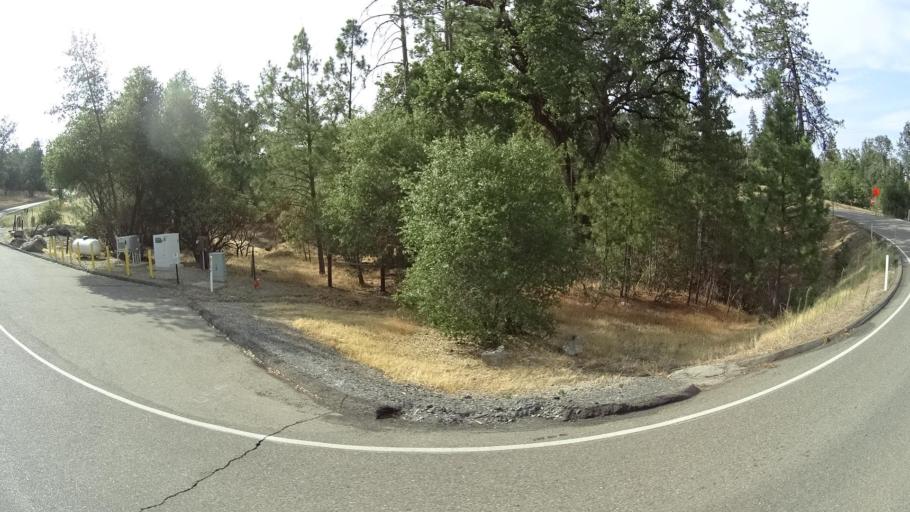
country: US
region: California
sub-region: Madera County
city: Ahwahnee
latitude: 37.4636
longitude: -119.7769
